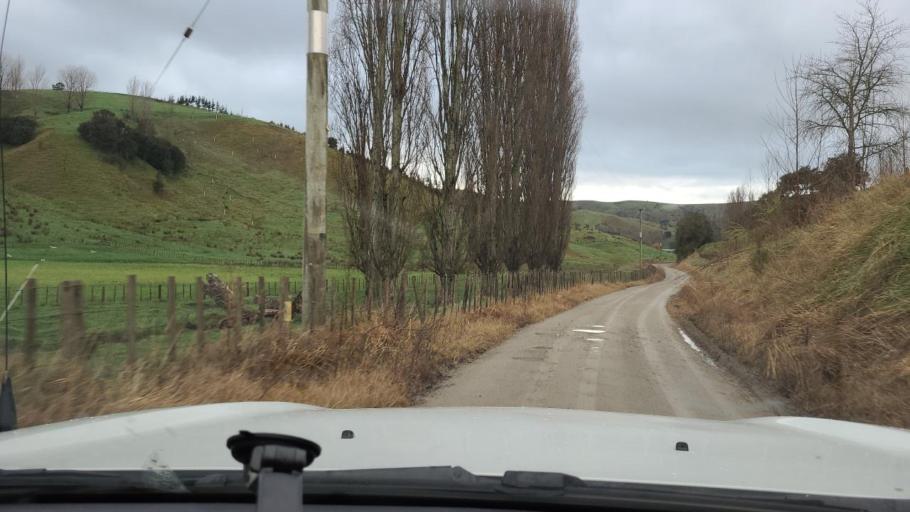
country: NZ
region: Gisborne
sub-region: Gisborne District
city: Gisborne
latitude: -38.5880
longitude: 177.8062
